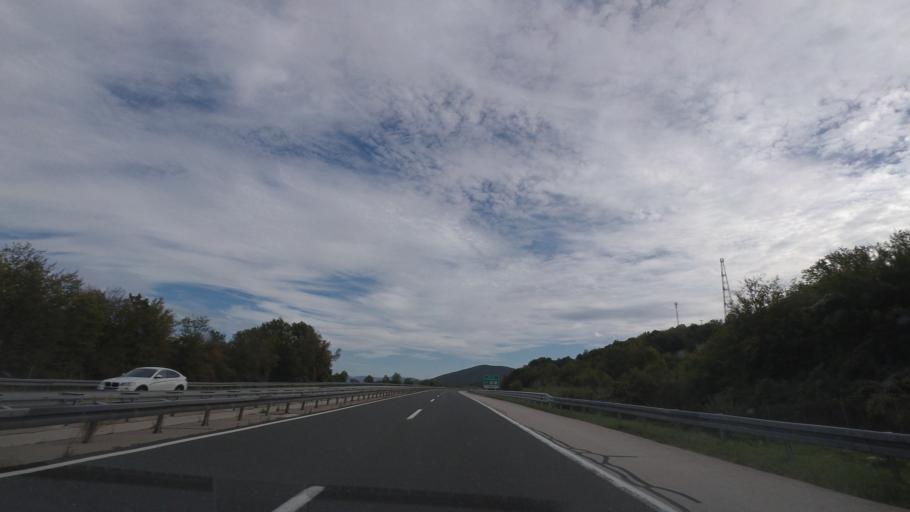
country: HR
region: Licko-Senjska
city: Brinje
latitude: 44.9424
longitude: 15.1654
